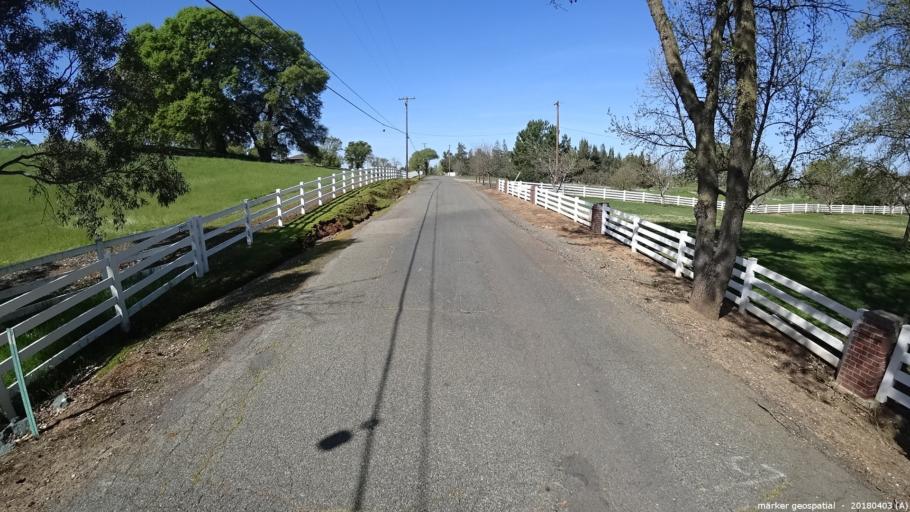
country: US
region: California
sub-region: Sacramento County
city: Wilton
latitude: 38.4205
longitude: -121.2133
